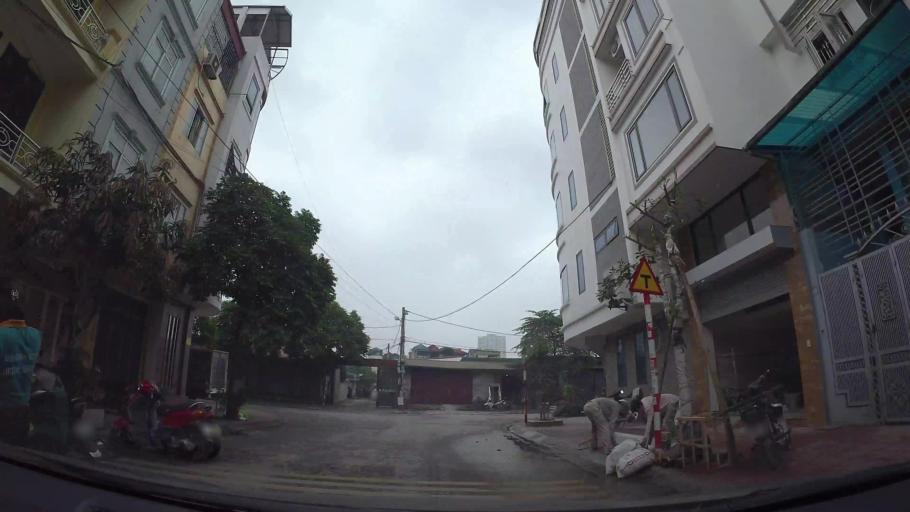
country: VN
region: Ha Noi
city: Van Dien
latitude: 20.9685
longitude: 105.8432
